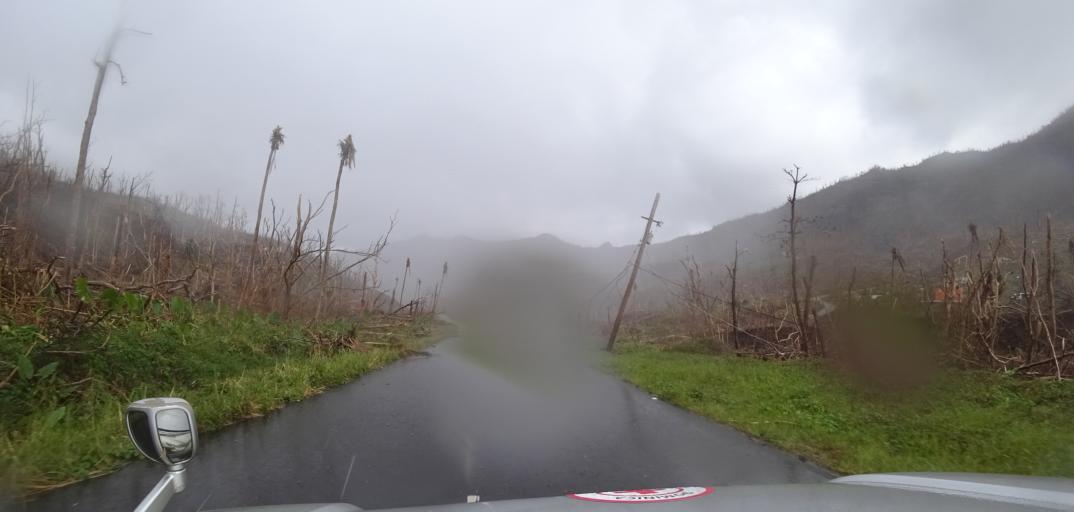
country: DM
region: Saint David
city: Castle Bruce
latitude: 15.4833
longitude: -61.2806
